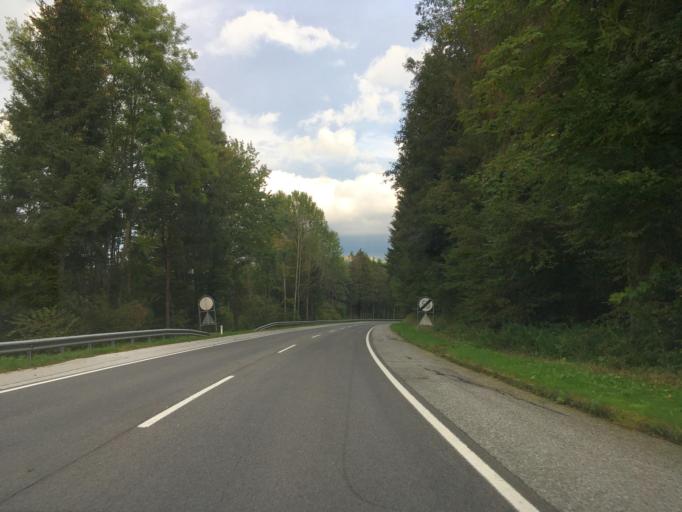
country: AT
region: Lower Austria
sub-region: Politischer Bezirk Neunkirchen
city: Monichkirchen
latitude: 47.5418
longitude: 16.0684
